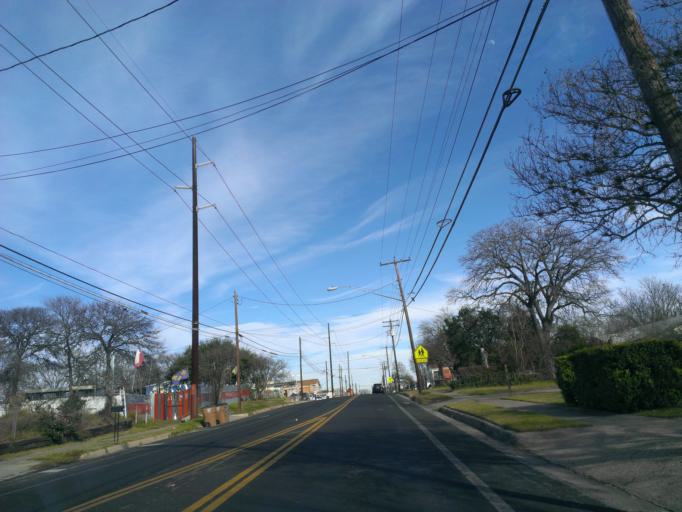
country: US
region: Texas
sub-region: Travis County
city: Austin
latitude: 30.2732
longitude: -97.7234
